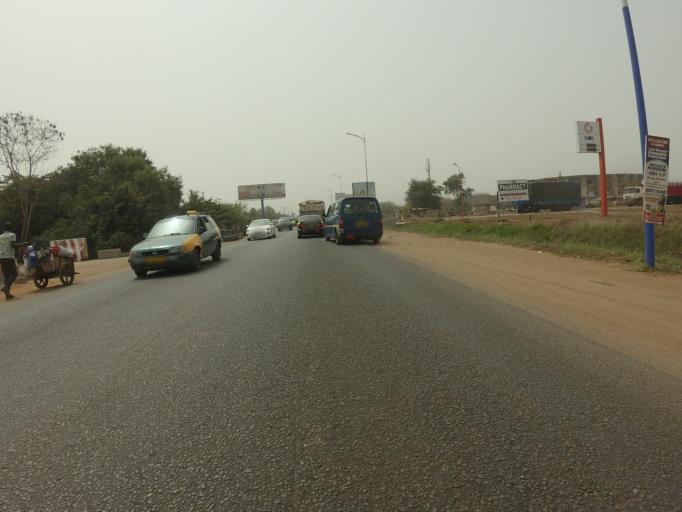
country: GH
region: Greater Accra
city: Tema
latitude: 5.7181
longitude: 0.0164
